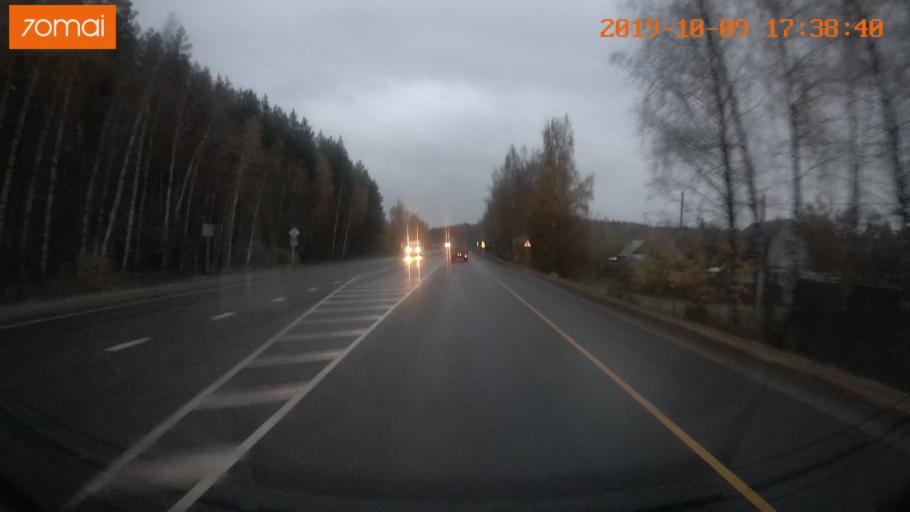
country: RU
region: Ivanovo
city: Bogorodskoye
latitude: 57.0686
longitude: 40.9517
